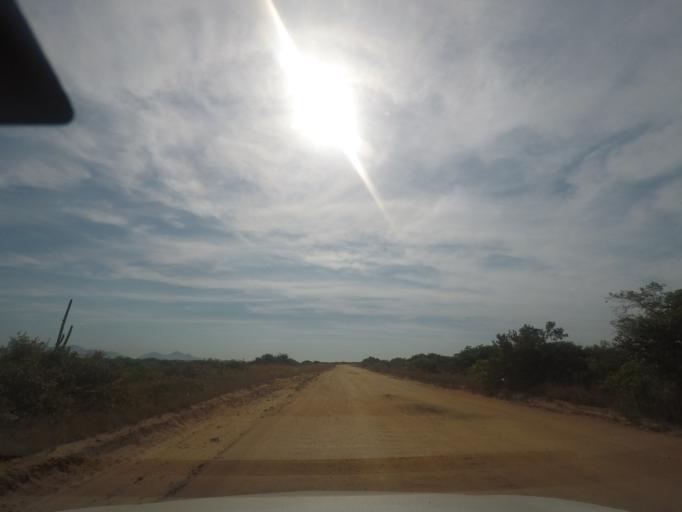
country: BR
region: Rio de Janeiro
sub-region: Marica
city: Marica
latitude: -22.9582
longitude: -42.8807
